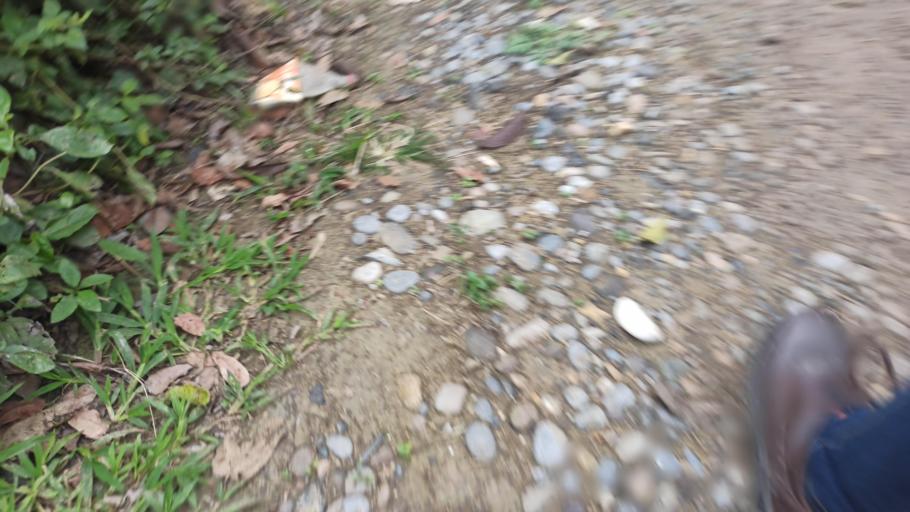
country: MX
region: Veracruz
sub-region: Coatzintla
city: Manuel Maria Contreras
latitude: 20.3513
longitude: -97.4650
